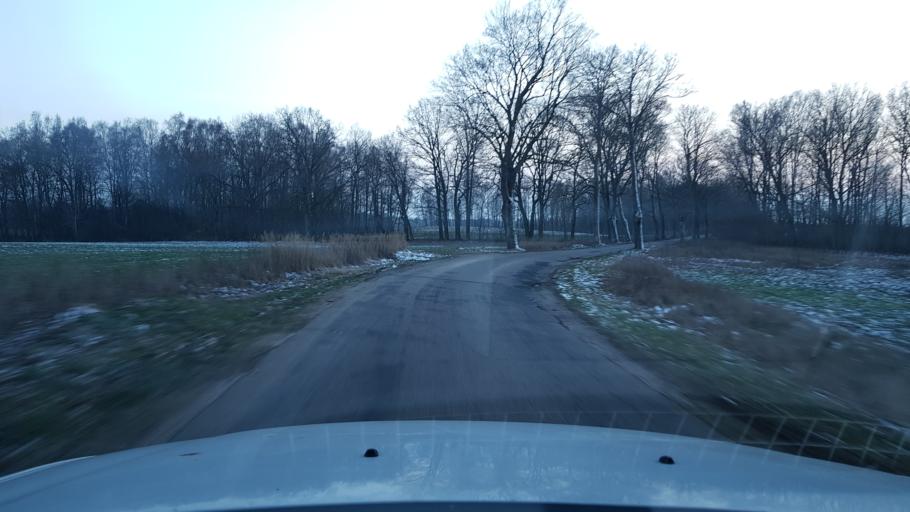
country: PL
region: West Pomeranian Voivodeship
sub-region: Powiat bialogardzki
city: Karlino
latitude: 54.0172
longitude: 15.8477
